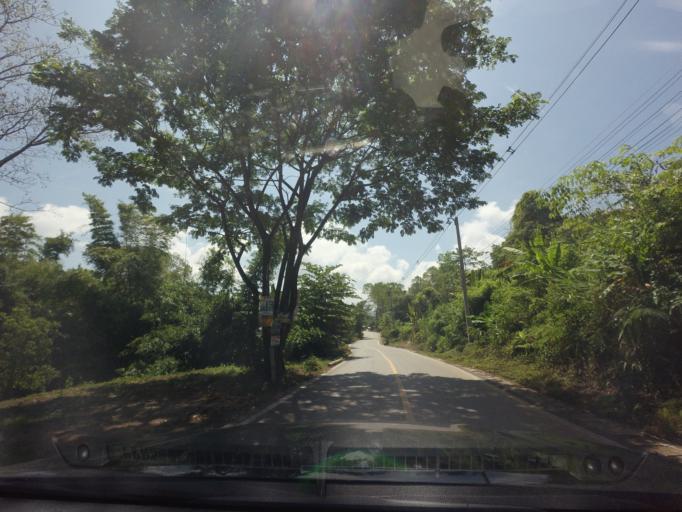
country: TH
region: Phetchabun
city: Khao Kho
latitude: 16.7854
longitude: 101.0483
